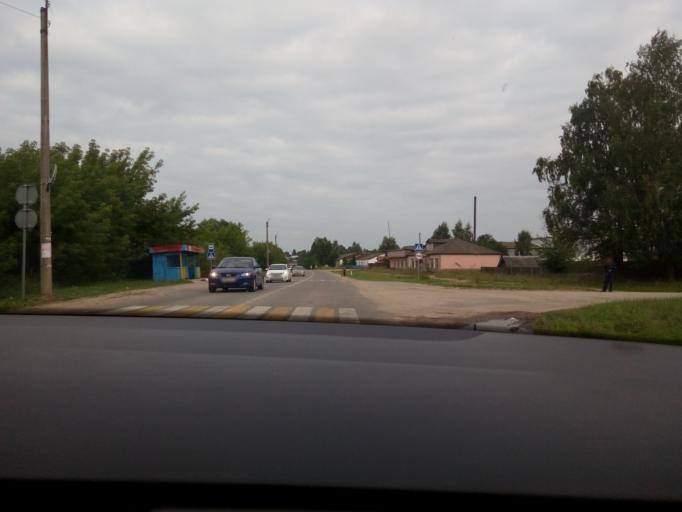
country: RU
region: Nizjnij Novgorod
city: Voskresenskoye
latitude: 56.8112
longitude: 45.4434
